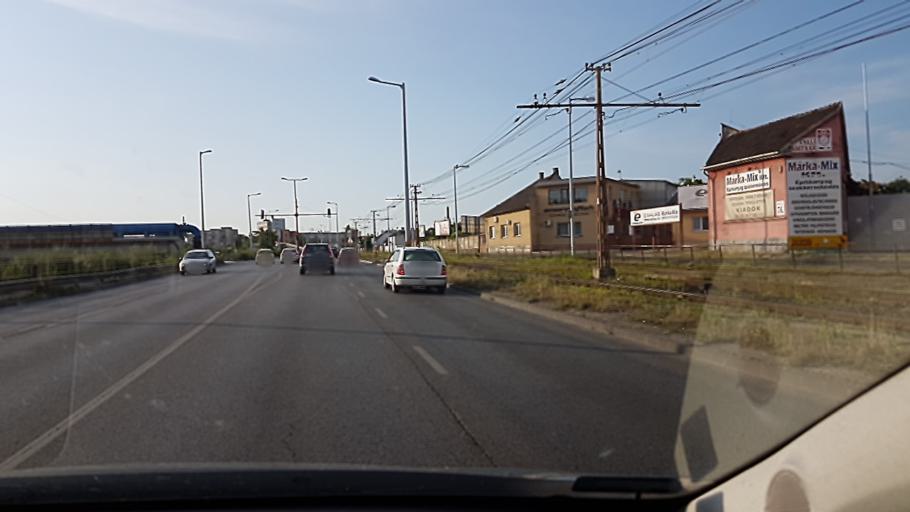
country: HU
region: Budapest
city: Budapest XX. keruelet
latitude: 47.4256
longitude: 19.1038
